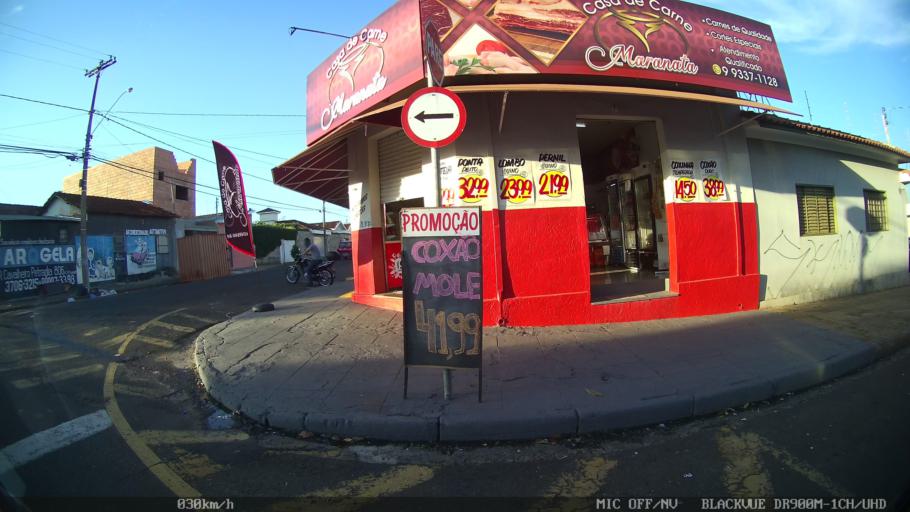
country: BR
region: Sao Paulo
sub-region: Franca
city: Franca
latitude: -20.5292
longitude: -47.3896
